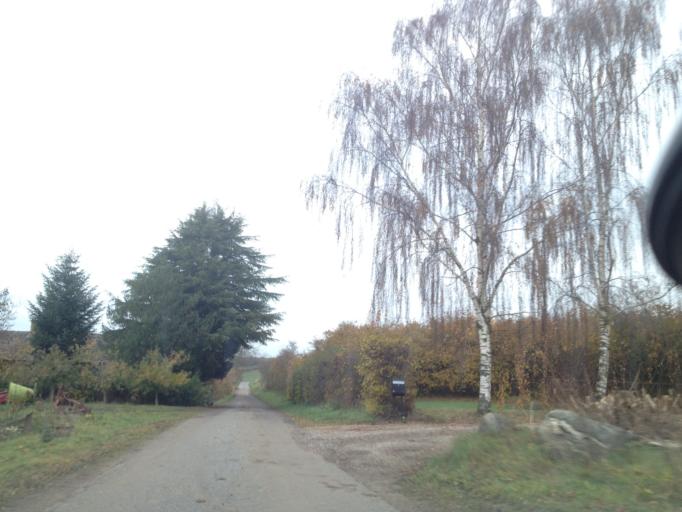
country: DK
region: South Denmark
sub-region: Assens Kommune
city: Vissenbjerg
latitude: 55.4144
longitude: 10.1558
